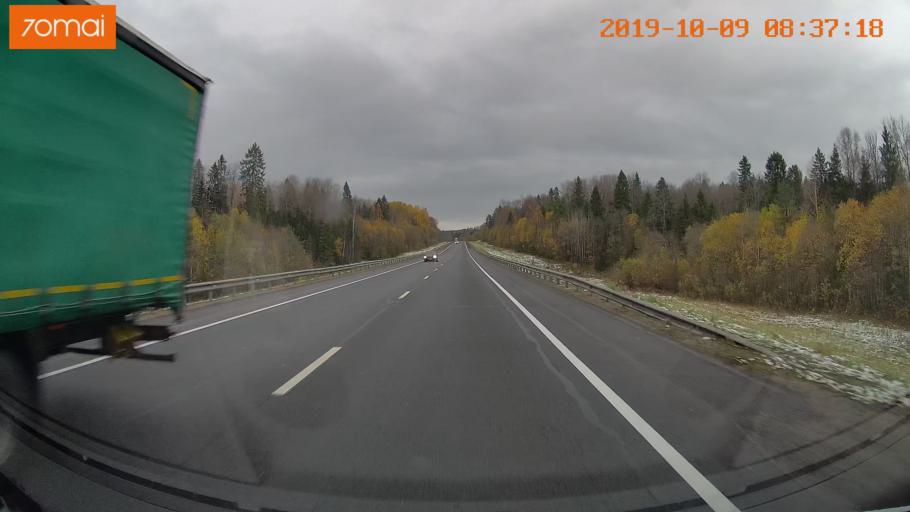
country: RU
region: Vologda
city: Gryazovets
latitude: 58.9394
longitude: 40.1749
